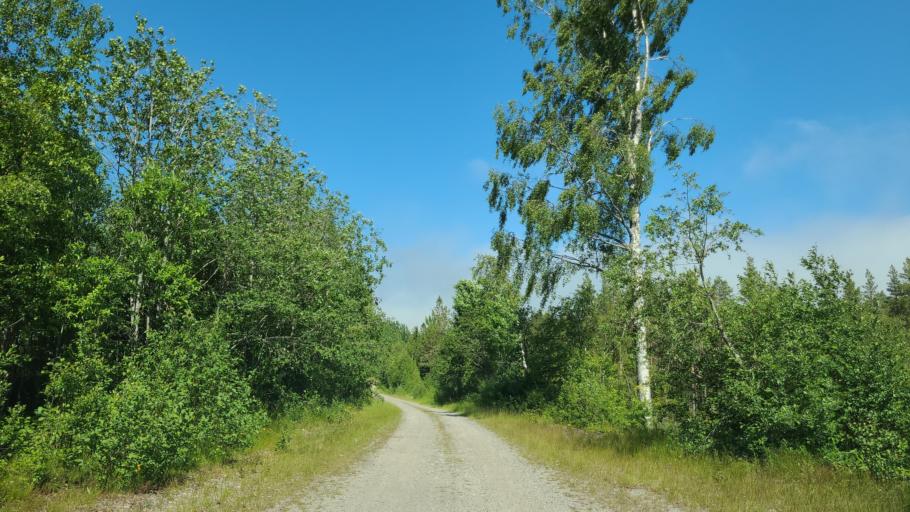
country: SE
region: Vaesternorrland
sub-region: OErnskoeldsviks Kommun
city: Husum
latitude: 63.4452
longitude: 19.2362
